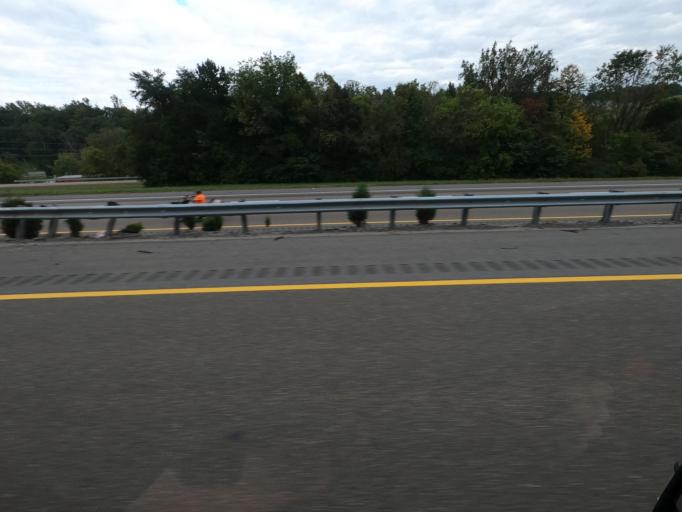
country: US
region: Tennessee
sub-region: Jefferson County
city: Dandridge
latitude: 36.0232
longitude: -83.4734
